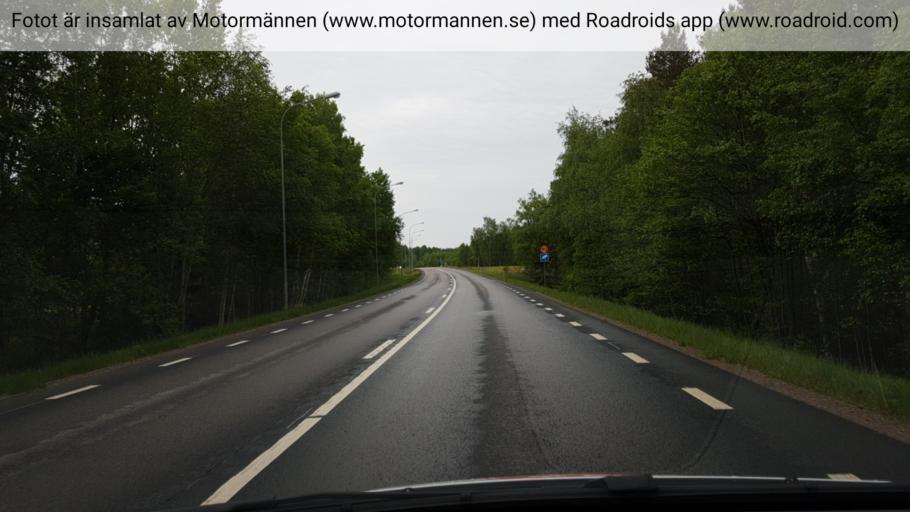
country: SE
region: Kalmar
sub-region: Vimmerby Kommun
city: Vimmerby
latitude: 57.5900
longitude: 15.8477
